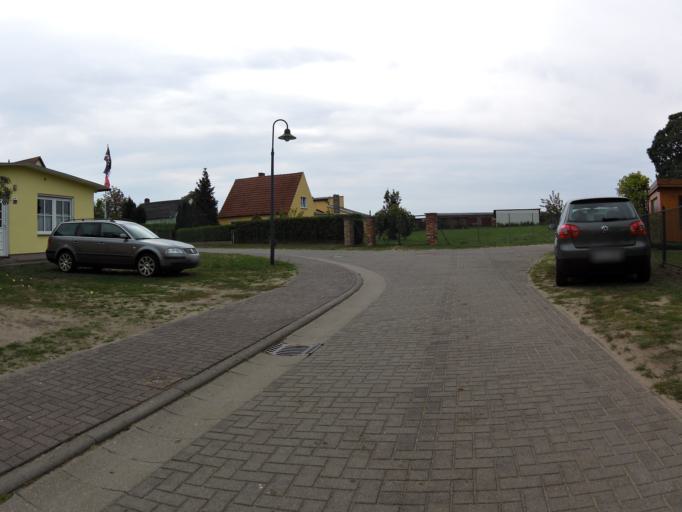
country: DE
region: Mecklenburg-Vorpommern
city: Seebad Heringsdorf
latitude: 53.8804
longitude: 14.1692
